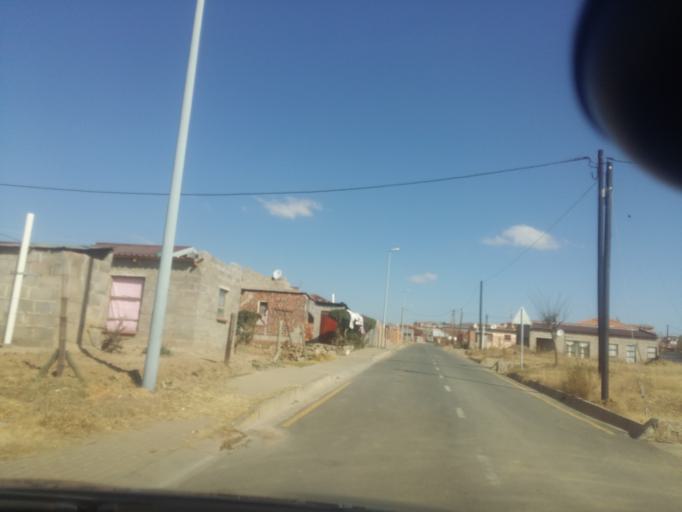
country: LS
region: Maseru
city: Maseru
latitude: -29.3409
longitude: 27.4524
